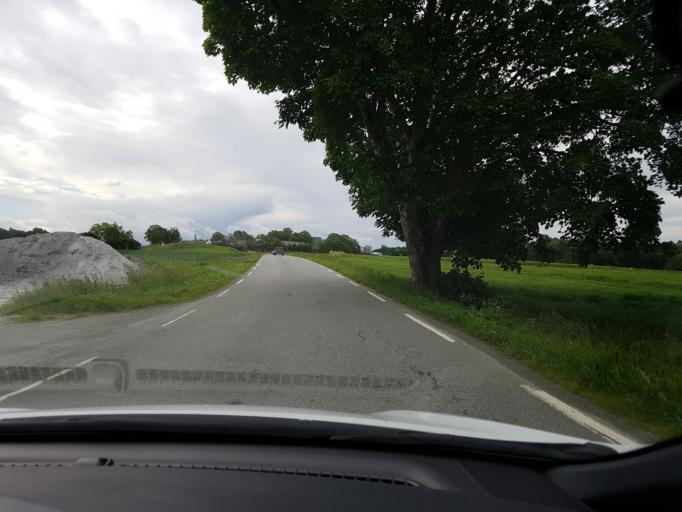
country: NO
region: Nord-Trondelag
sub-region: Frosta
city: Frosta
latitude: 63.5709
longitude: 10.7050
